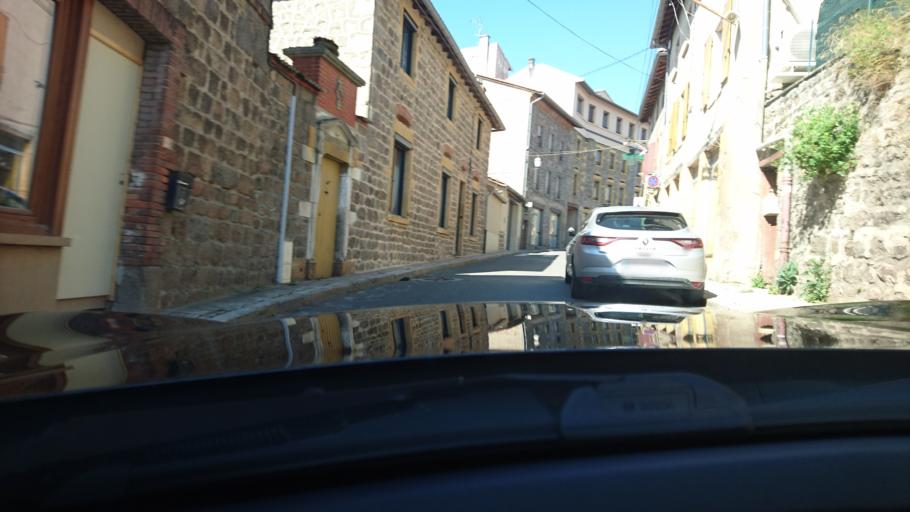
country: FR
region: Rhone-Alpes
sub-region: Departement du Rhone
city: Montrottier
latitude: 45.7899
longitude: 4.4674
